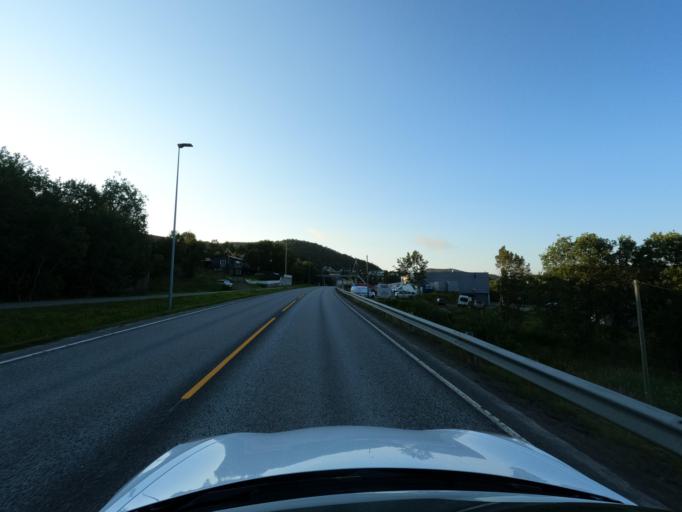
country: NO
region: Troms
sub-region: Harstad
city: Harstad
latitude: 68.7694
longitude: 16.5581
